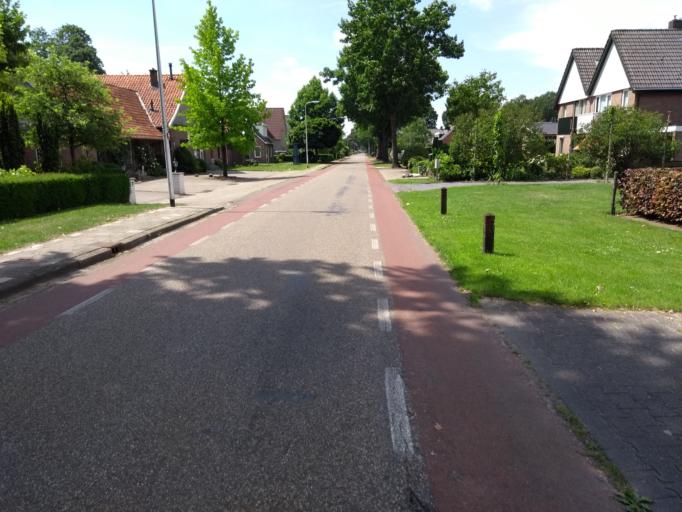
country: NL
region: Overijssel
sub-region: Gemeente Twenterand
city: Vriezenveen
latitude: 52.3740
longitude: 6.6278
